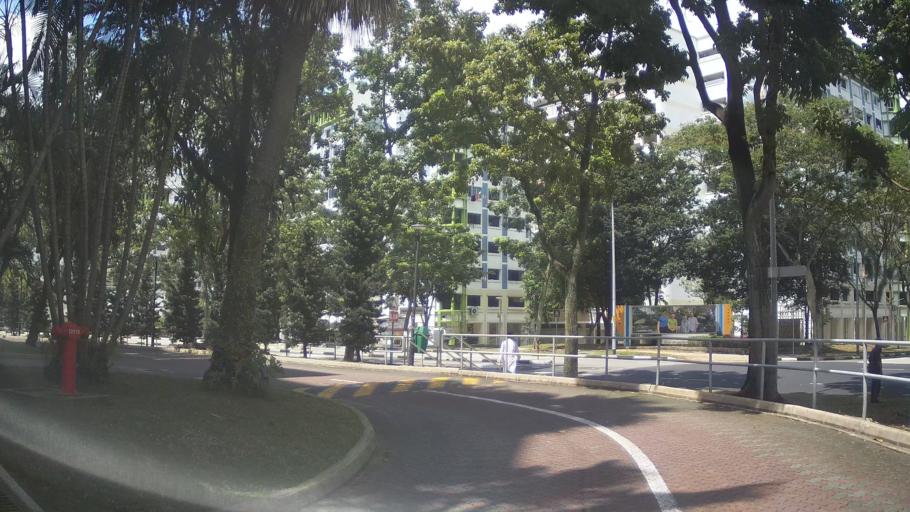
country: MY
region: Johor
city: Johor Bahru
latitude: 1.3380
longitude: 103.7205
